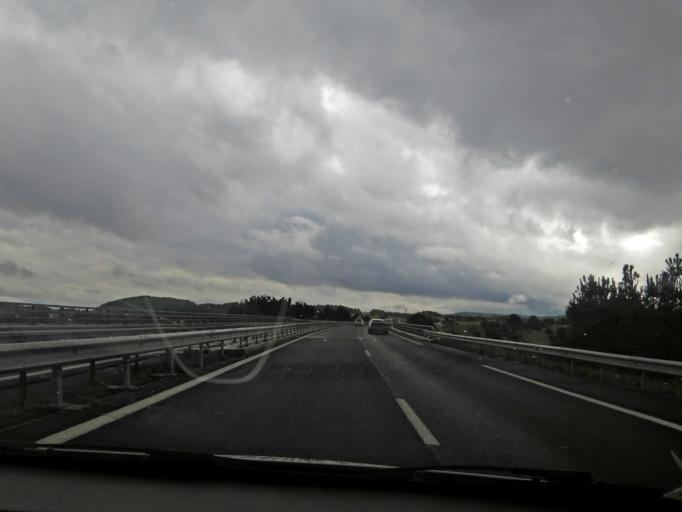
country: FR
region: Languedoc-Roussillon
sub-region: Departement de la Lozere
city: Le Malzieu-Ville
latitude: 44.9054
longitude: 3.2288
